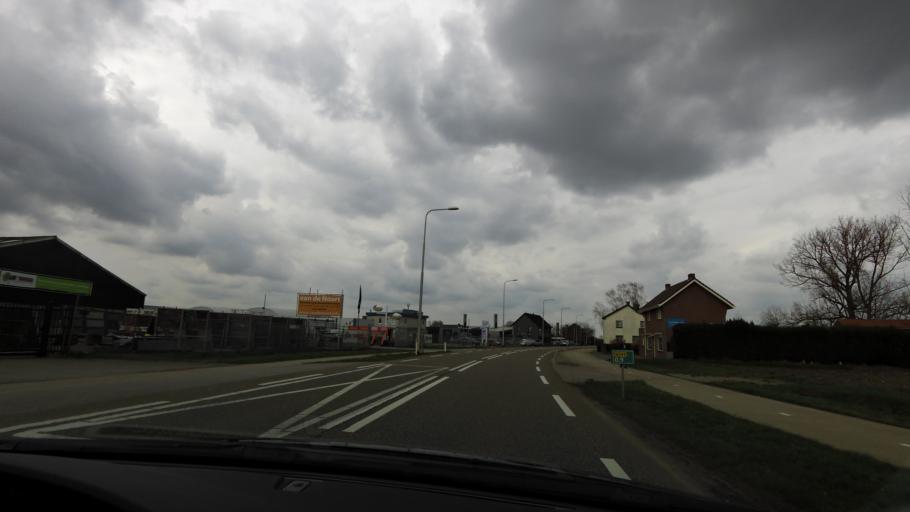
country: NL
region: Limburg
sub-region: Gemeente Sittard-Geleen
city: Born
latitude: 51.0702
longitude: 5.8452
